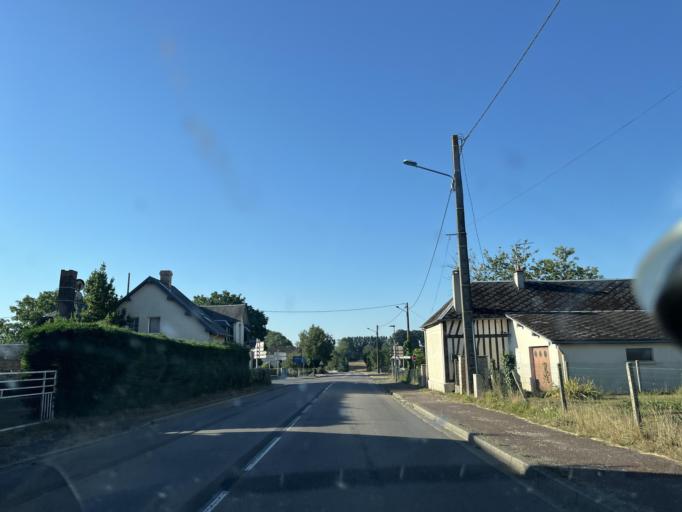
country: FR
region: Haute-Normandie
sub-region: Departement de la Seine-Maritime
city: Lanquetot
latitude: 49.5735
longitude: 0.5999
